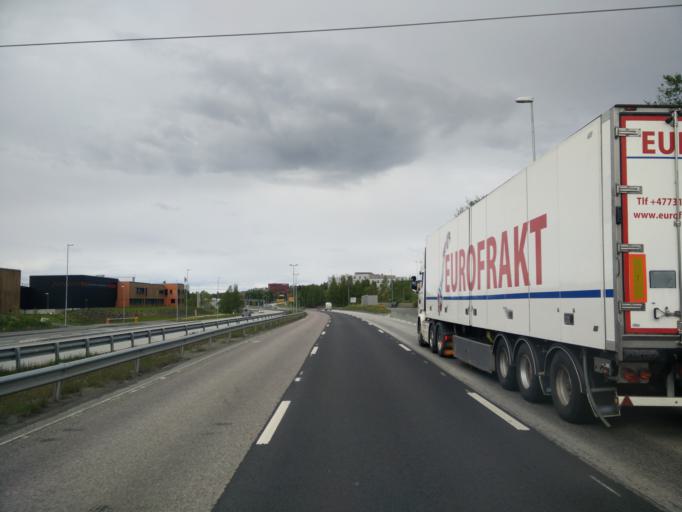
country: NO
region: Sor-Trondelag
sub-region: Trondheim
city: Trondheim
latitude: 63.3950
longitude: 10.3898
